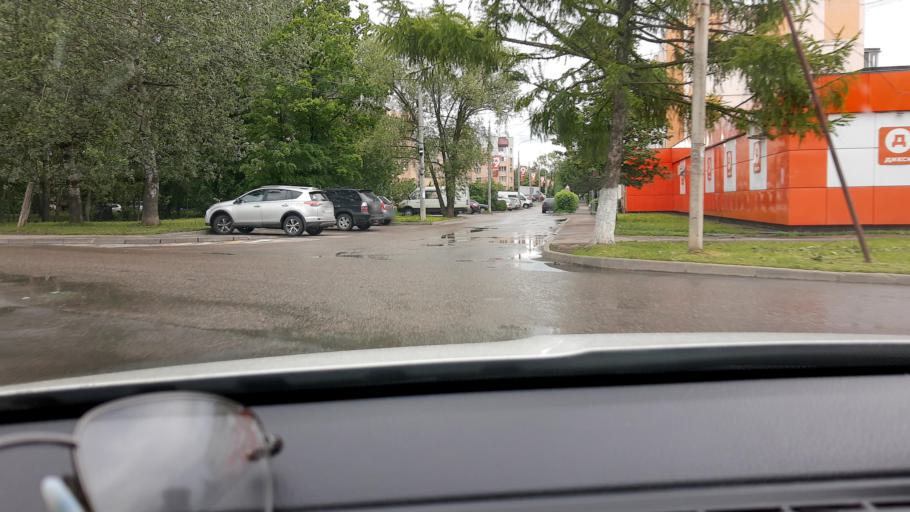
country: RU
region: Moskovskaya
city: Gorki-Leninskiye
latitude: 55.5088
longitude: 37.7783
